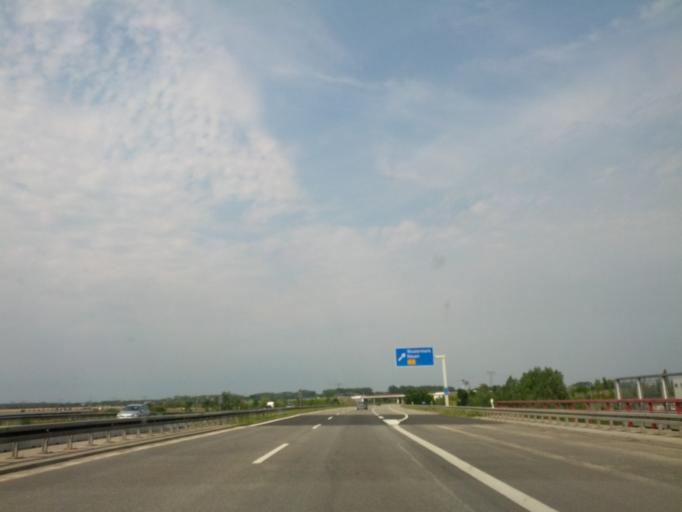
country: DE
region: Brandenburg
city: Wustermark
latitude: 52.5504
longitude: 12.9637
